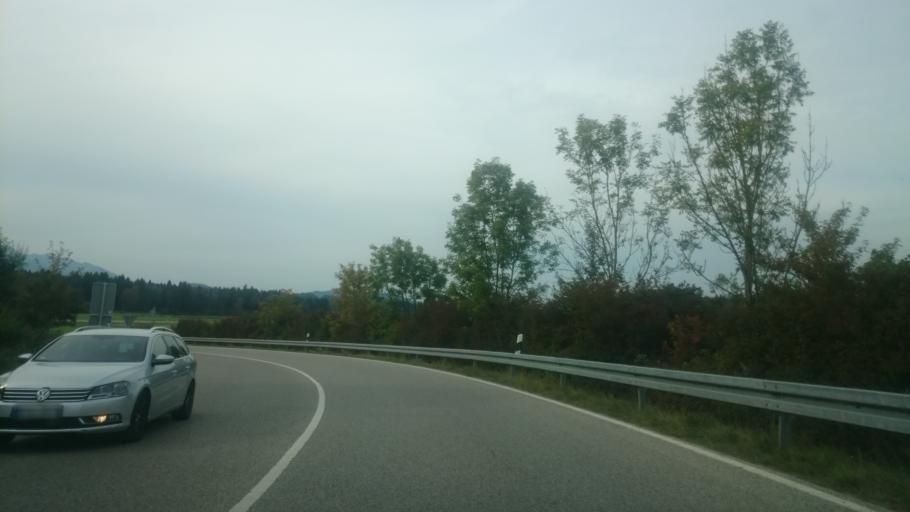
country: DE
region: Bavaria
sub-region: Swabia
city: Fuessen
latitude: 47.5802
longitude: 10.6788
